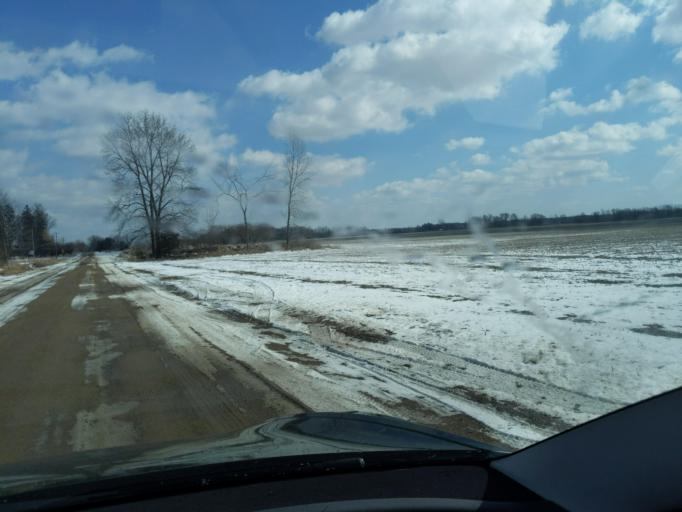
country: US
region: Michigan
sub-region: Livingston County
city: Fowlerville
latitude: 42.6139
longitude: -84.1052
